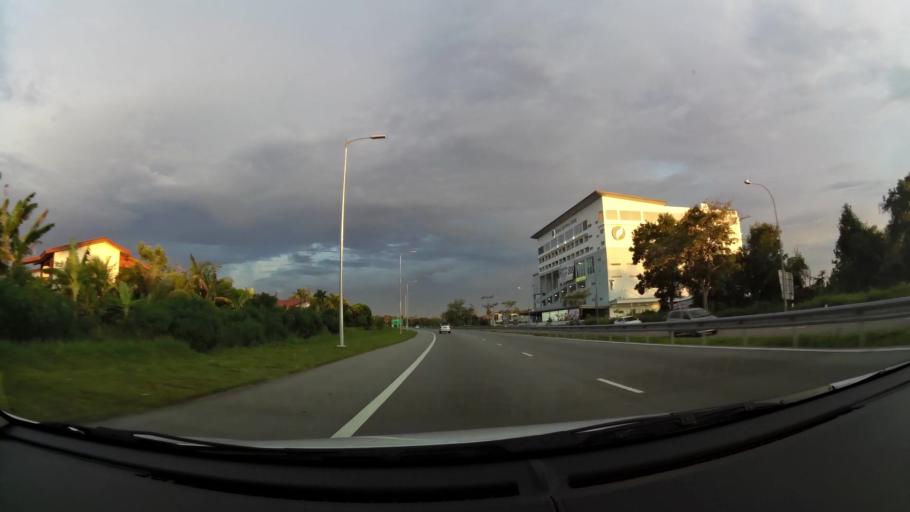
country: BN
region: Belait
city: Kuala Belait
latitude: 4.5737
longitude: 114.2218
